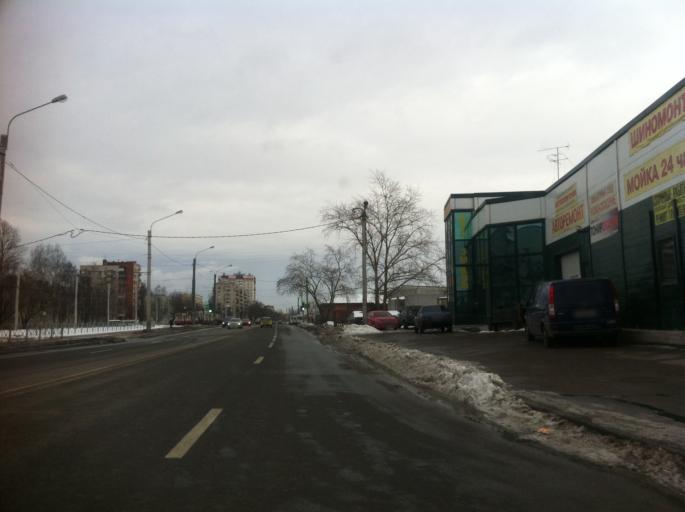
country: RU
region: St.-Petersburg
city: Sosnovaya Polyana
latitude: 59.8255
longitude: 30.1422
